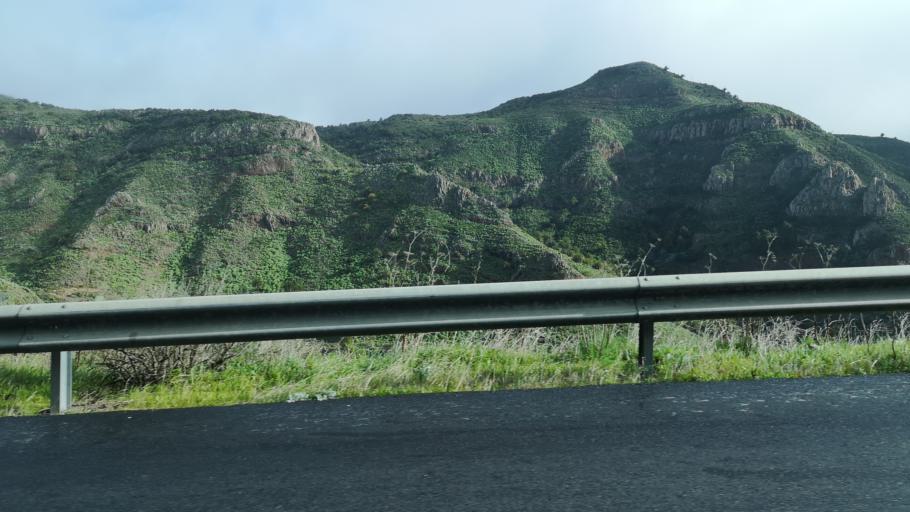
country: ES
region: Canary Islands
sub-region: Provincia de Santa Cruz de Tenerife
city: Alajero
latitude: 28.0920
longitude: -17.2020
